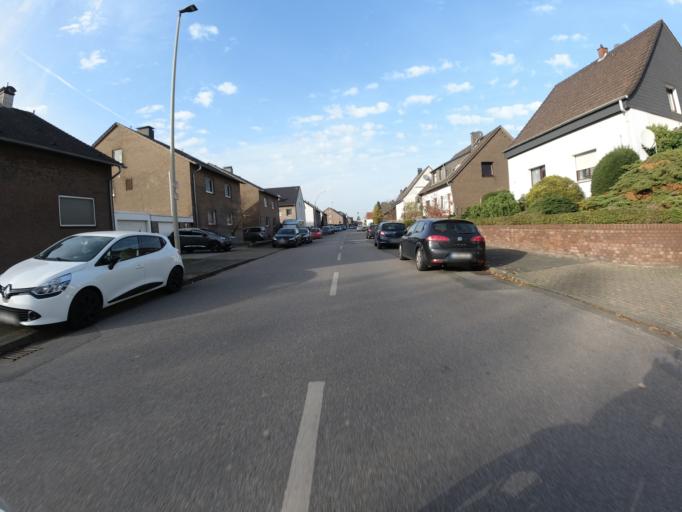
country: DE
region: North Rhine-Westphalia
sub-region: Regierungsbezirk Dusseldorf
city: Moers
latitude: 51.3936
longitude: 6.6723
